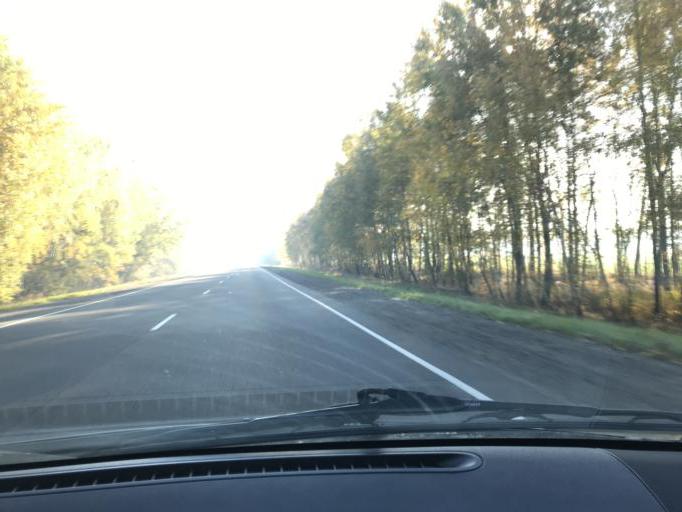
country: BY
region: Brest
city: Horad Luninyets
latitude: 52.2984
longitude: 26.7338
